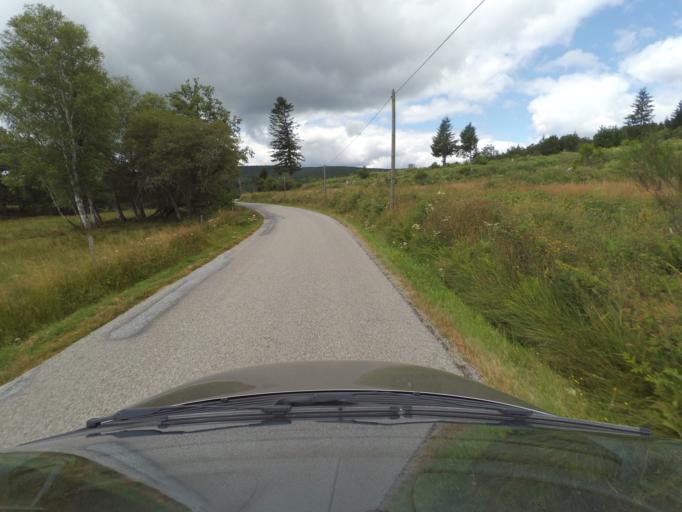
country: FR
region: Limousin
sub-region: Departement de la Haute-Vienne
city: Peyrat-le-Chateau
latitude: 45.8212
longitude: 1.9217
